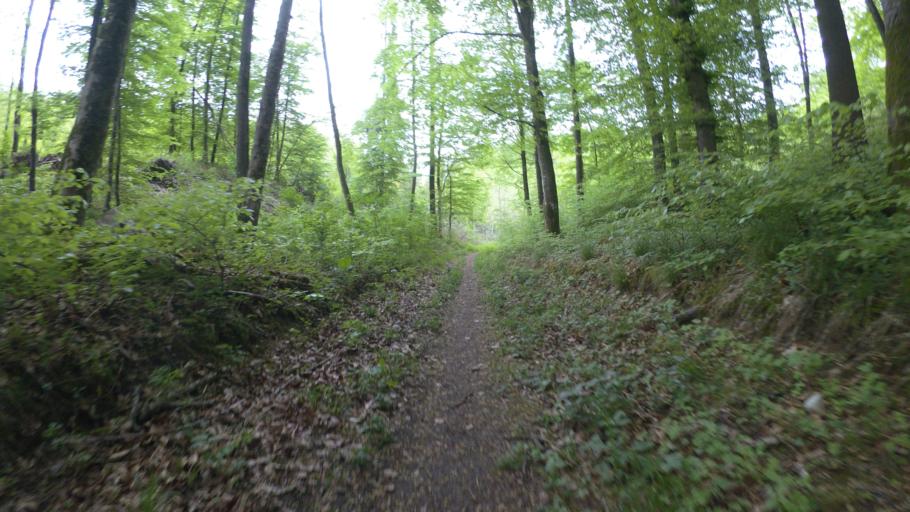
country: DE
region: Bavaria
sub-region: Upper Bavaria
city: Nussdorf
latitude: 47.9032
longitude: 12.6246
